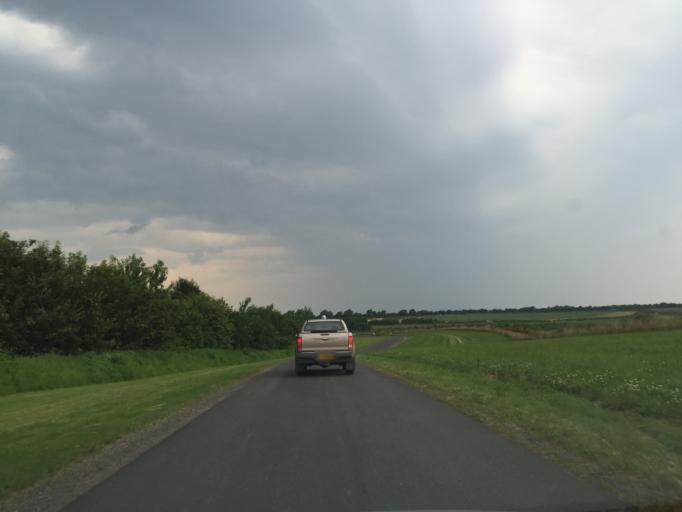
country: DK
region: Central Jutland
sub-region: Viborg Kommune
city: Bjerringbro
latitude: 56.3283
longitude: 9.6482
